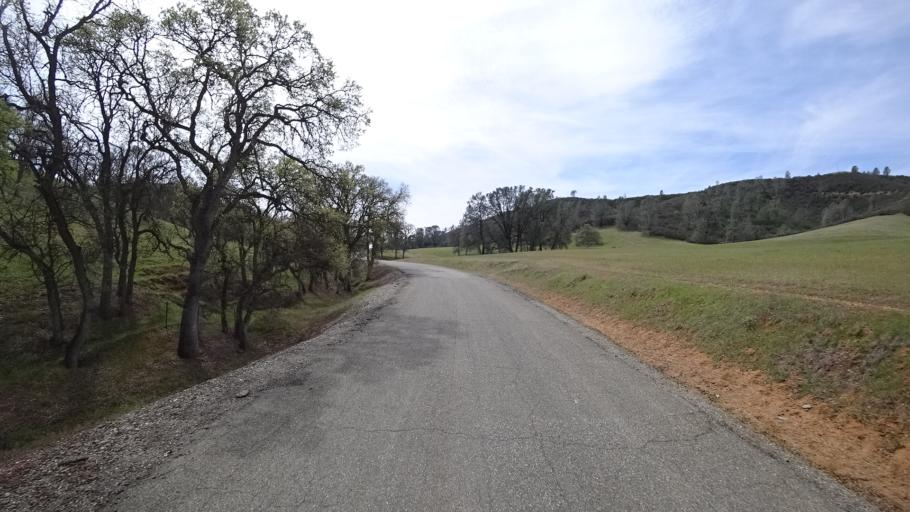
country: US
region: California
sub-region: Glenn County
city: Willows
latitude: 39.6026
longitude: -122.5273
